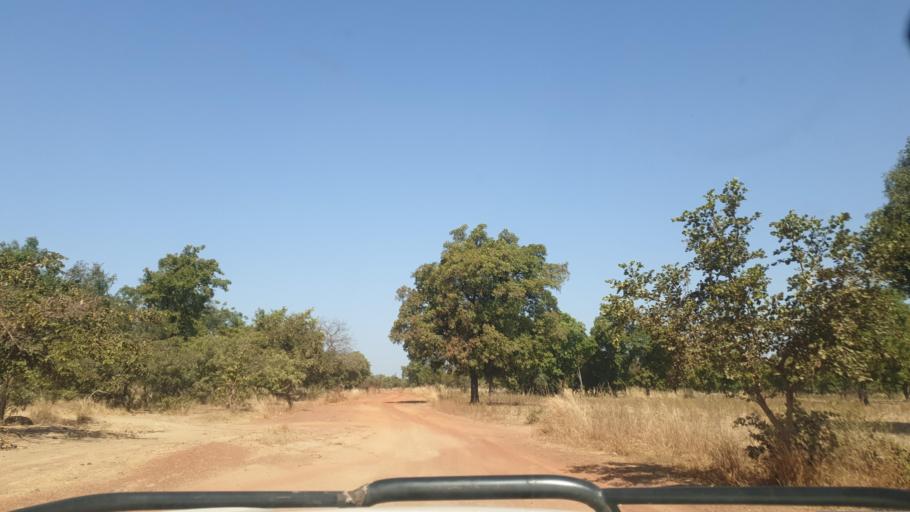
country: ML
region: Koulikoro
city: Dioila
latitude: 11.8982
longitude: -6.9809
